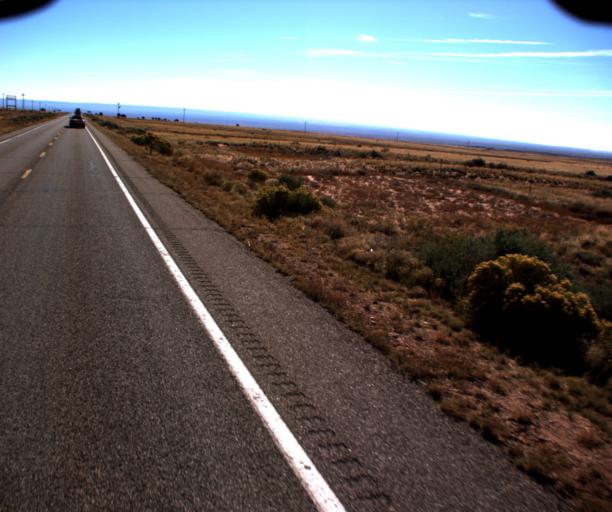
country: US
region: Arizona
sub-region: Mohave County
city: Colorado City
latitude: 36.8645
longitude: -112.8323
